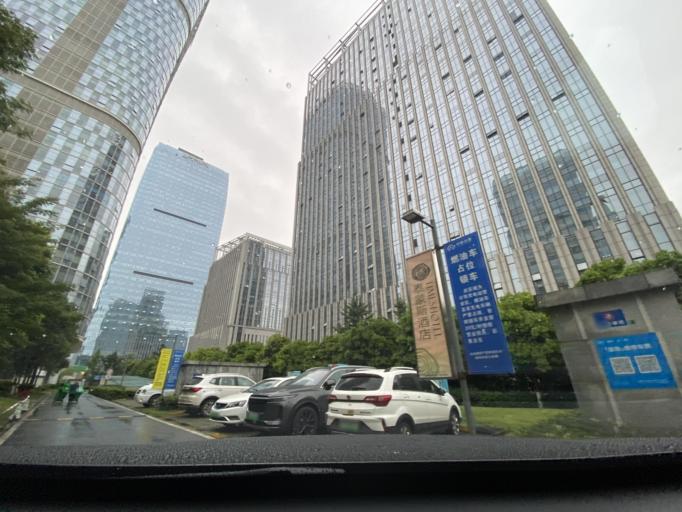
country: CN
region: Sichuan
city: Chengdu
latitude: 30.5433
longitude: 104.0613
